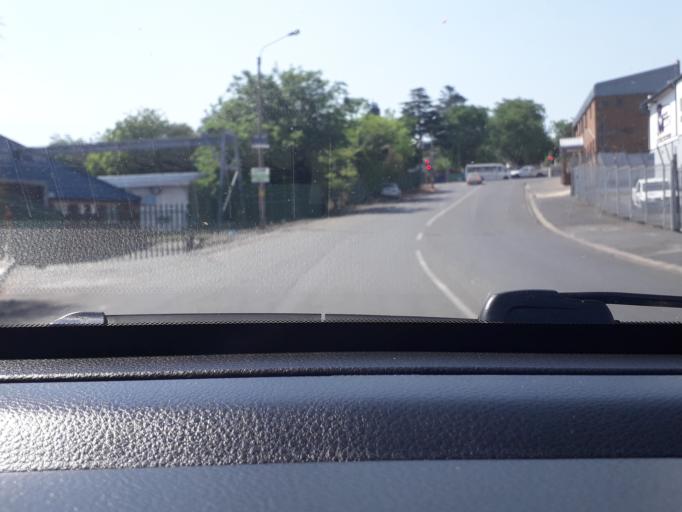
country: ZA
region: Gauteng
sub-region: City of Johannesburg Metropolitan Municipality
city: Modderfontein
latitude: -26.1290
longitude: 28.1516
